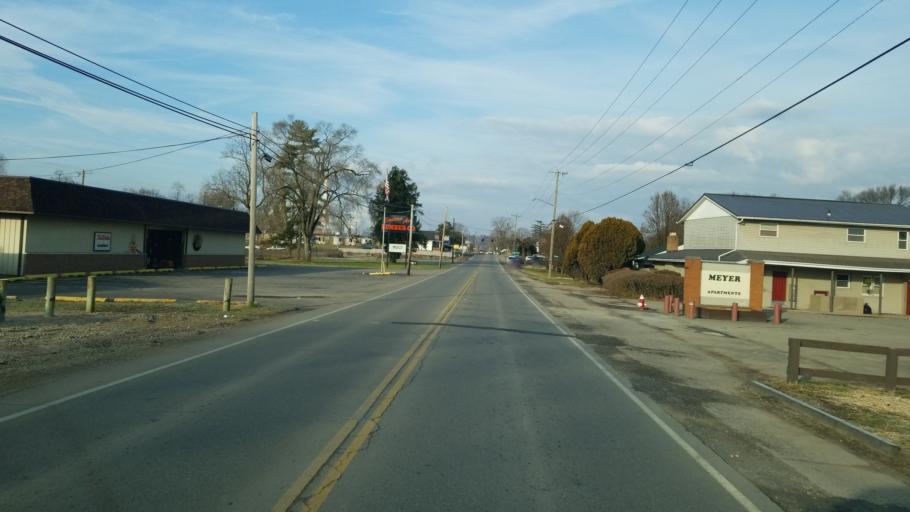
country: US
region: Ohio
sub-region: Ross County
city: Chillicothe
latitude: 39.3235
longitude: -82.9569
